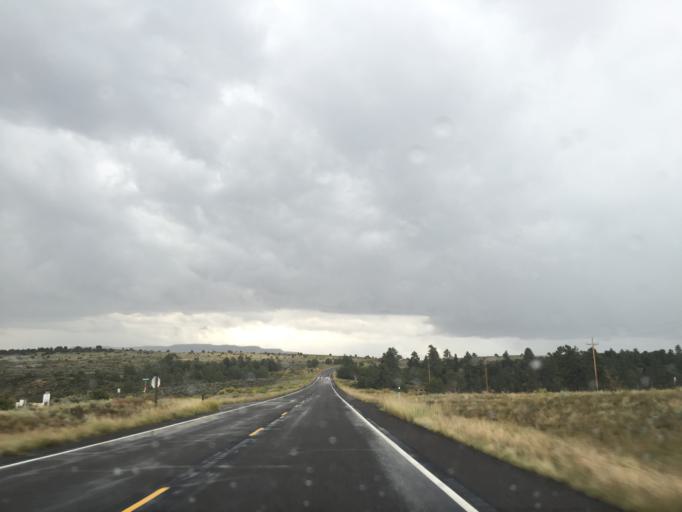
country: US
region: Utah
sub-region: Kane County
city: Kanab
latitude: 37.2338
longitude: -112.7376
